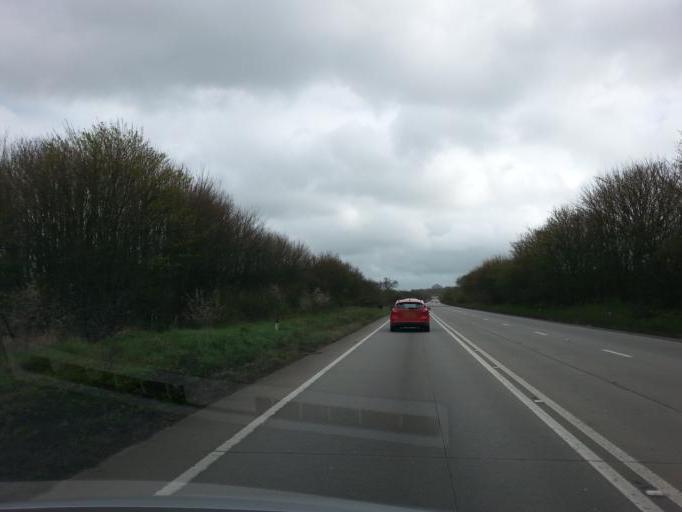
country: GB
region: England
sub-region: Somerset
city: Ilminster
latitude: 50.9400
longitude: -2.8841
